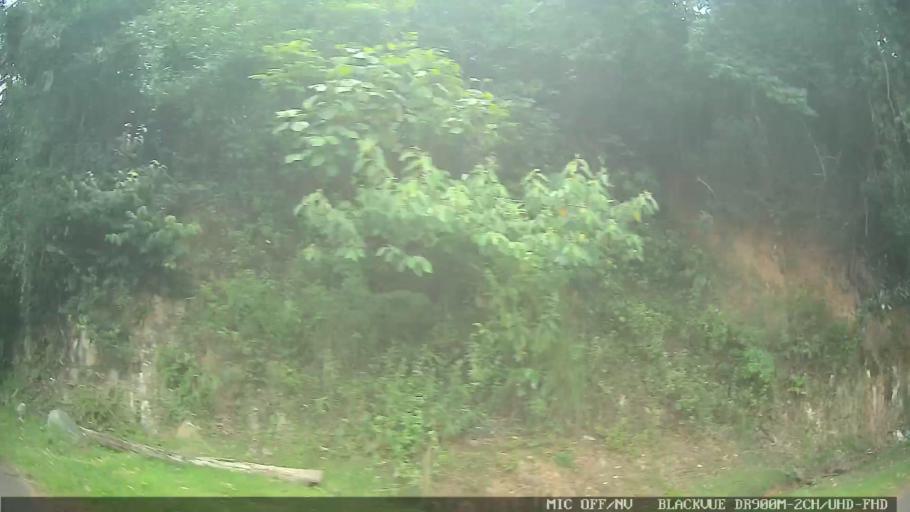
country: BR
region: Sao Paulo
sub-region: Atibaia
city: Atibaia
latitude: -23.0514
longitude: -46.5058
